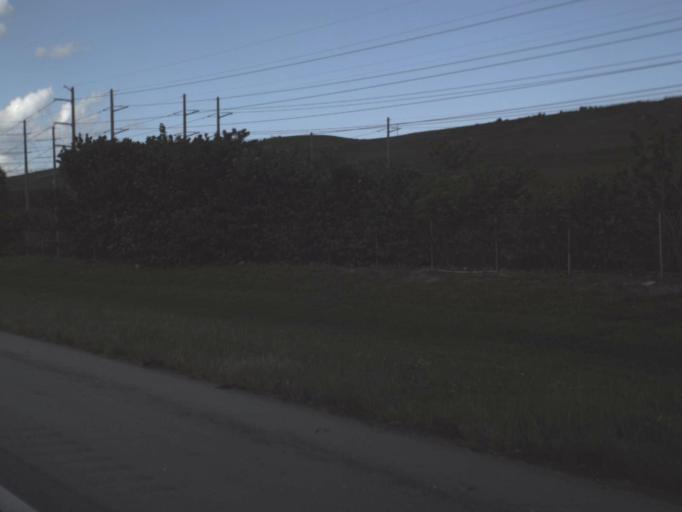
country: US
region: Florida
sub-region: Broward County
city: Coconut Creek
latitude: 26.2782
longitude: -80.1688
